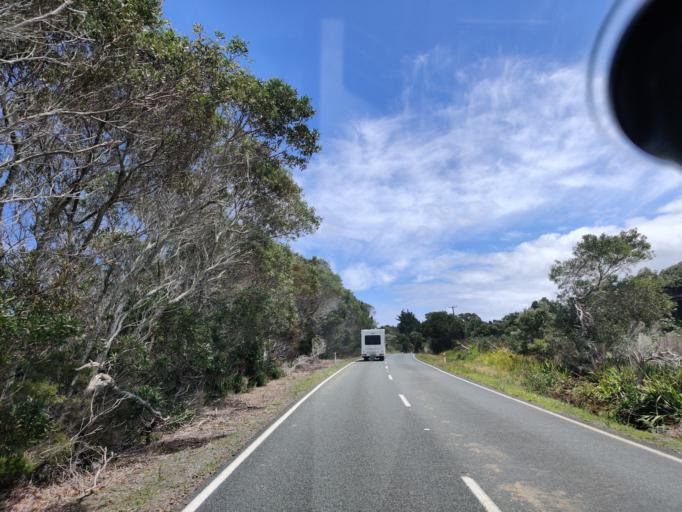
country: NZ
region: Northland
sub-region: Far North District
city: Kaitaia
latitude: -34.7469
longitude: 173.0499
